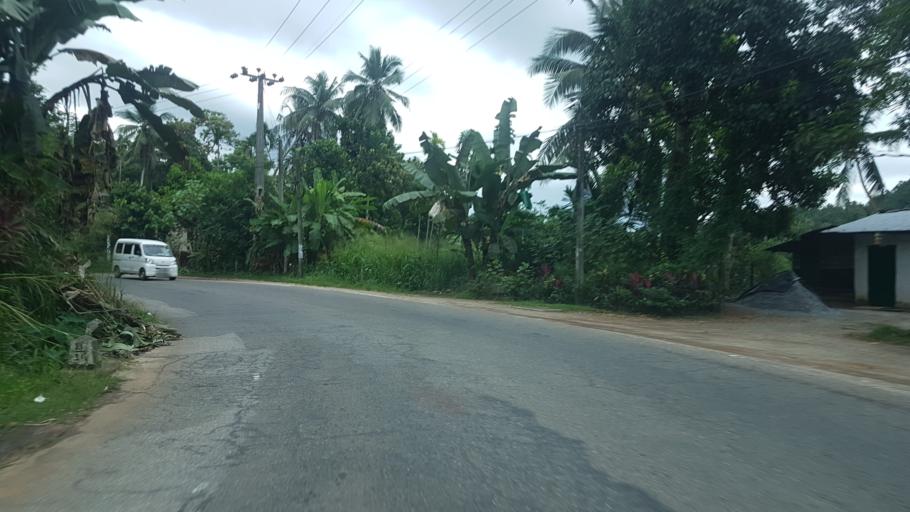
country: LK
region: Western
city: Hanwella Ihala
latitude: 7.0258
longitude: 80.2755
